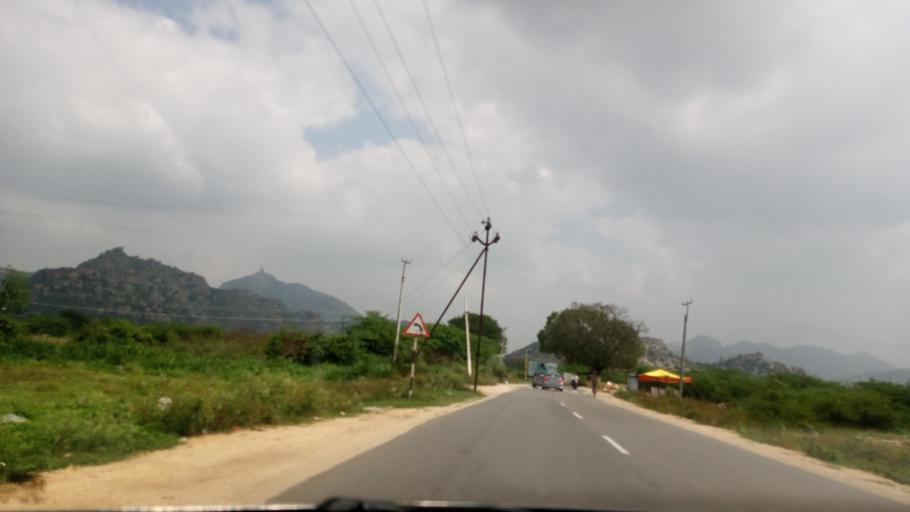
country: IN
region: Andhra Pradesh
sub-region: Chittoor
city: Madanapalle
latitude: 13.6423
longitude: 78.5575
